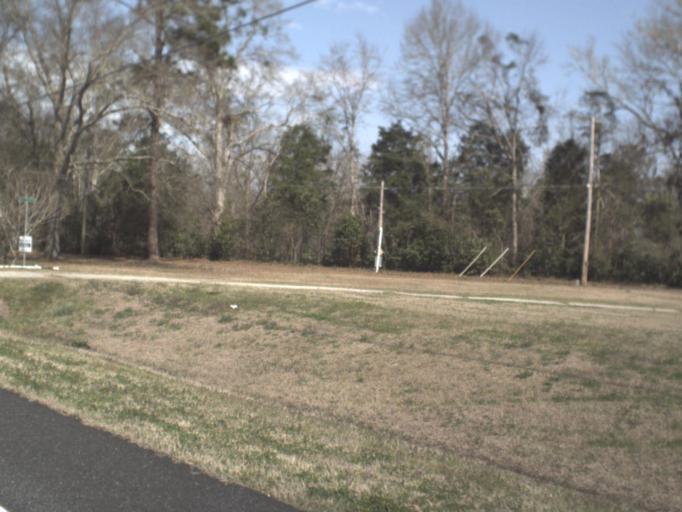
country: US
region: Florida
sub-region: Gadsden County
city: Havana
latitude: 30.5902
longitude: -84.4054
